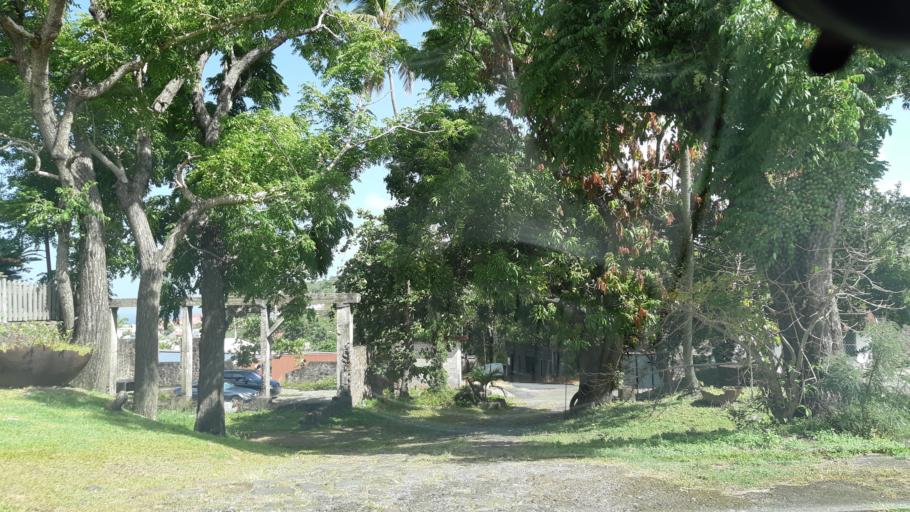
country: GP
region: Guadeloupe
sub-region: Guadeloupe
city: Basse-Terre
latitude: 16.0008
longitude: -61.7156
